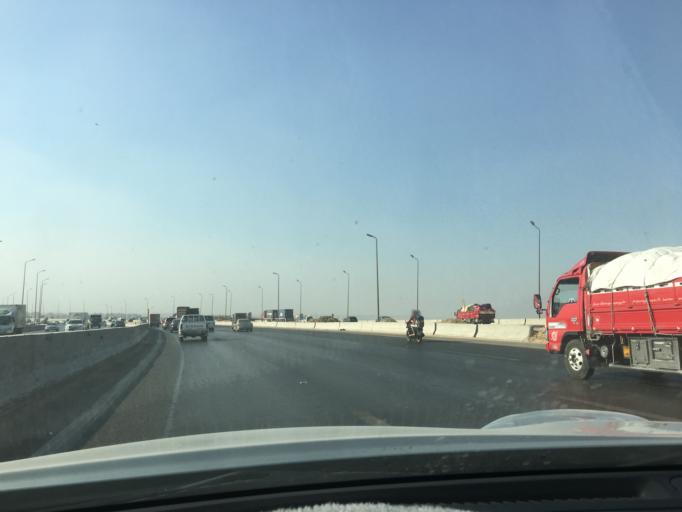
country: EG
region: Muhafazat al Qalyubiyah
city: Al Khankah
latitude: 30.1277
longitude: 31.4650
